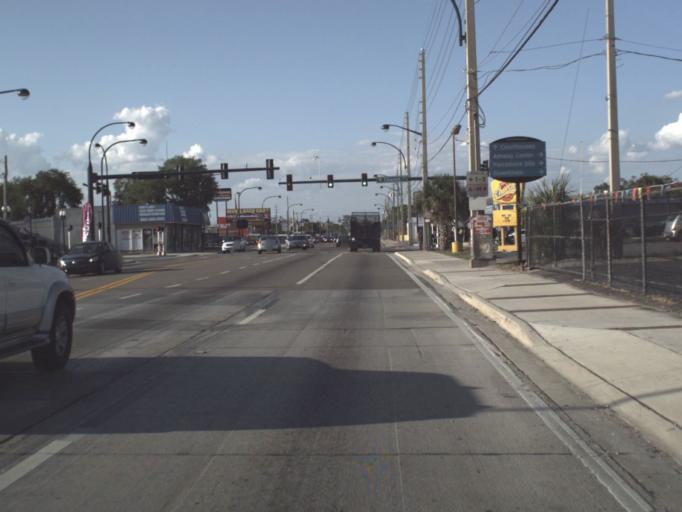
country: US
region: Florida
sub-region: Orange County
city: Orlando
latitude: 28.5394
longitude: -81.3972
